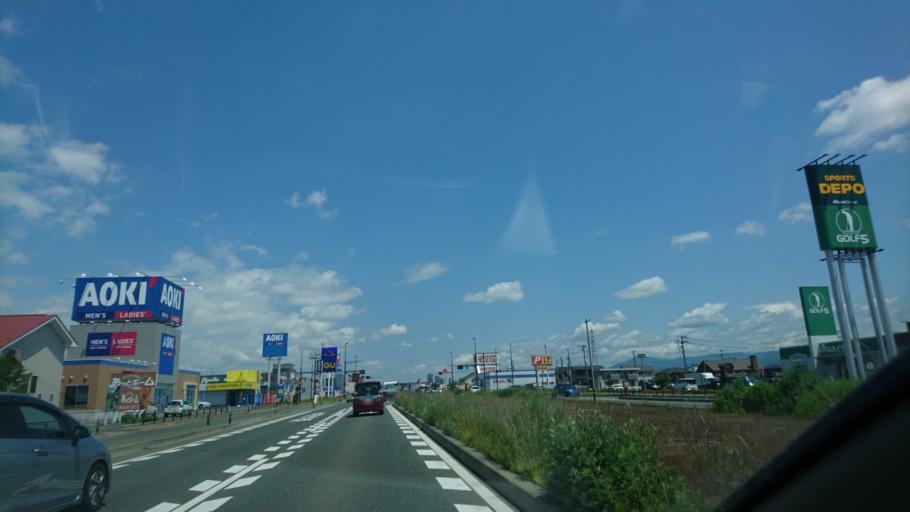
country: JP
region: Iwate
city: Morioka-shi
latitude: 39.6765
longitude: 141.1351
